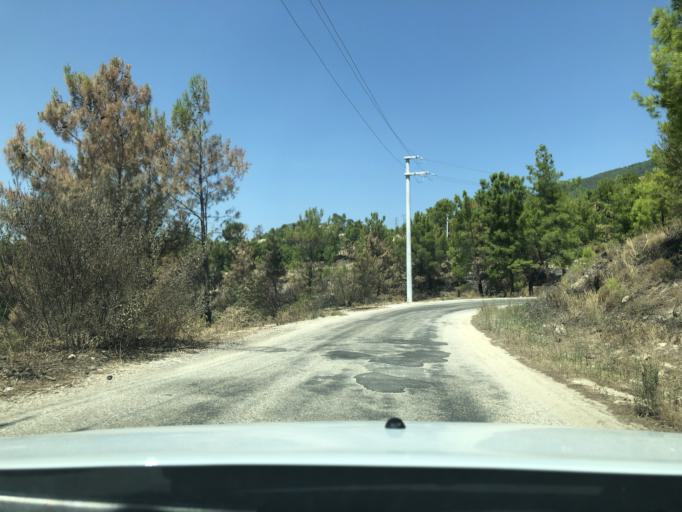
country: TR
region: Antalya
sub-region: Manavgat
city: Kizilagac
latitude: 36.8665
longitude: 31.5580
